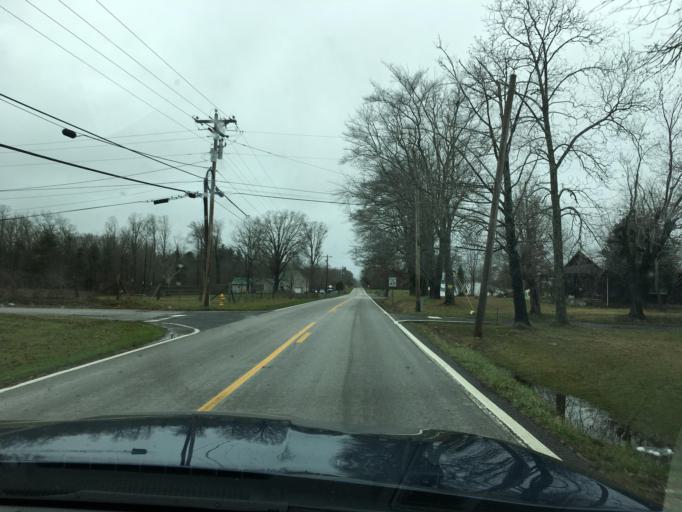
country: US
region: Tennessee
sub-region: Rhea County
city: Spring City
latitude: 35.7463
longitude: -84.8417
